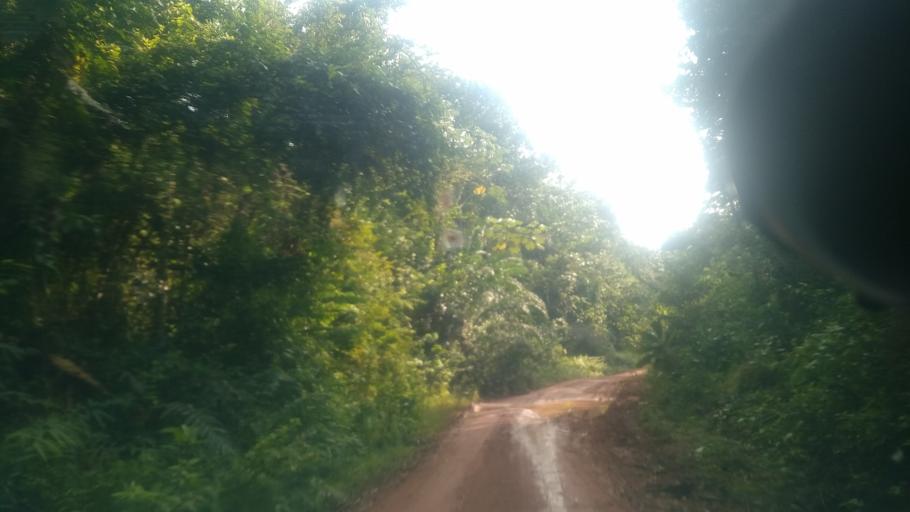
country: CM
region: South Province
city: Kribi
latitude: 2.6463
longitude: 9.8490
